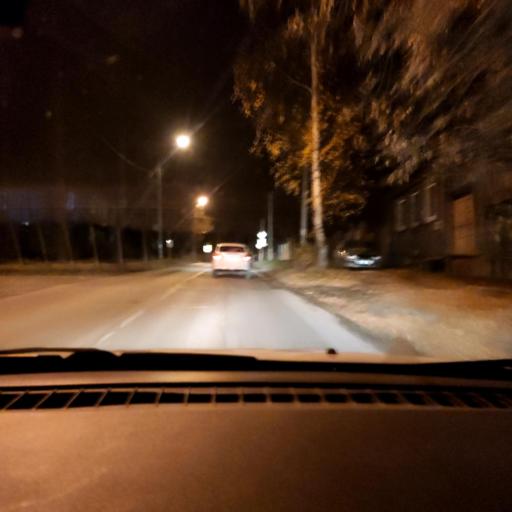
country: RU
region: Perm
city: Perm
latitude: 58.0391
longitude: 56.3285
